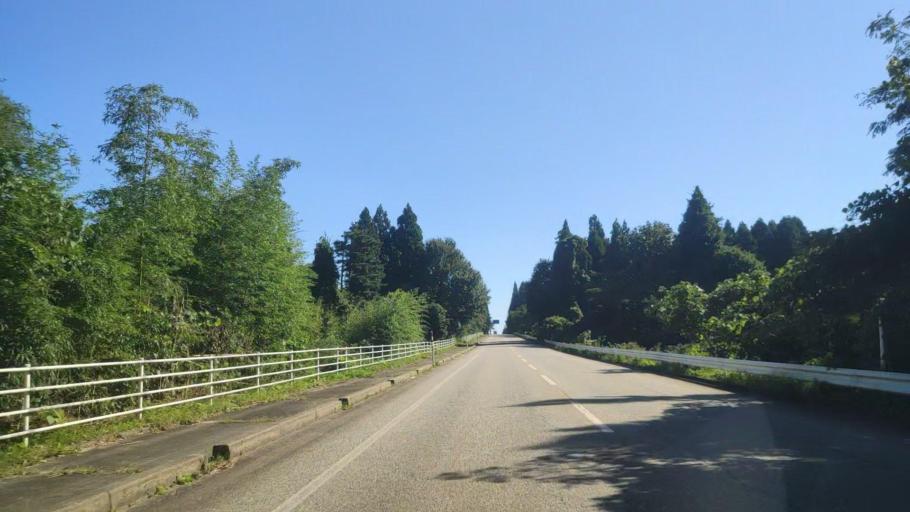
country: JP
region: Ishikawa
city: Nanao
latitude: 37.3726
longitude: 137.2351
